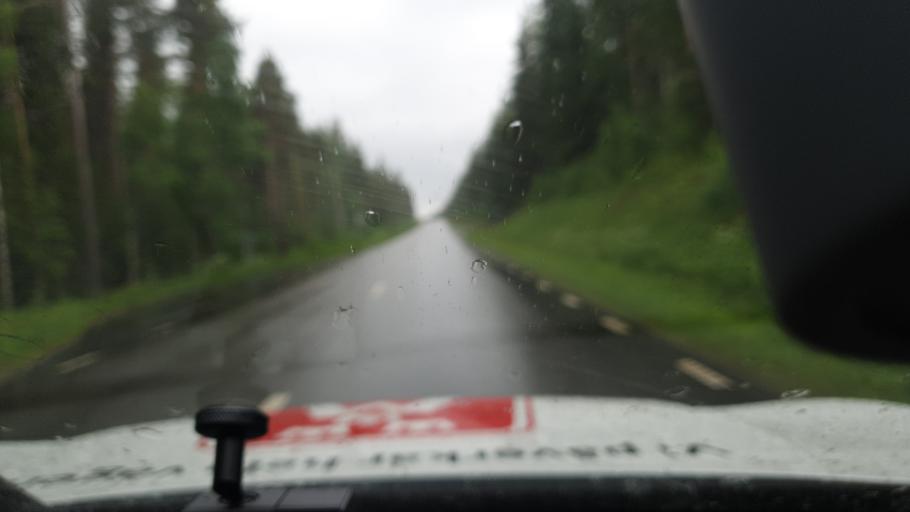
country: SE
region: Vaesterbotten
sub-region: Lycksele Kommun
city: Lycksele
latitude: 64.5534
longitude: 18.7333
